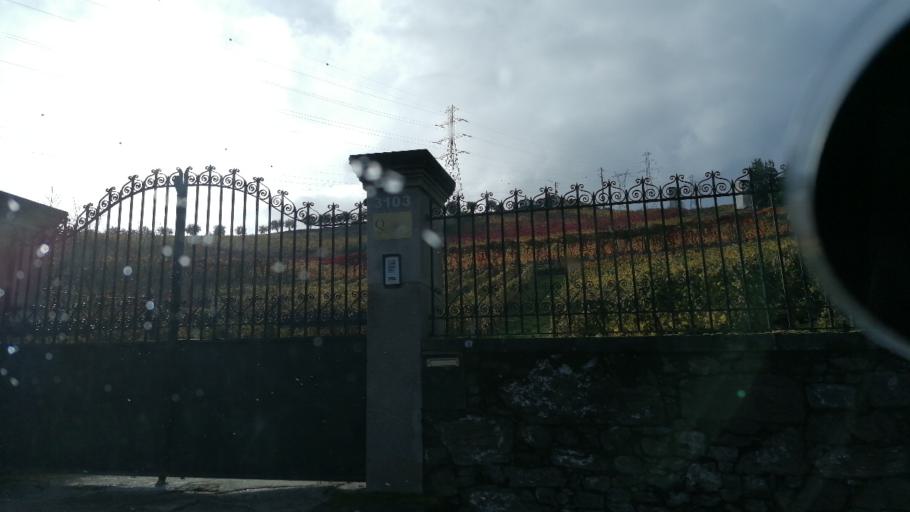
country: PT
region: Vila Real
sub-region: Peso da Regua
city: Peso da Regua
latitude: 41.1449
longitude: -7.7805
